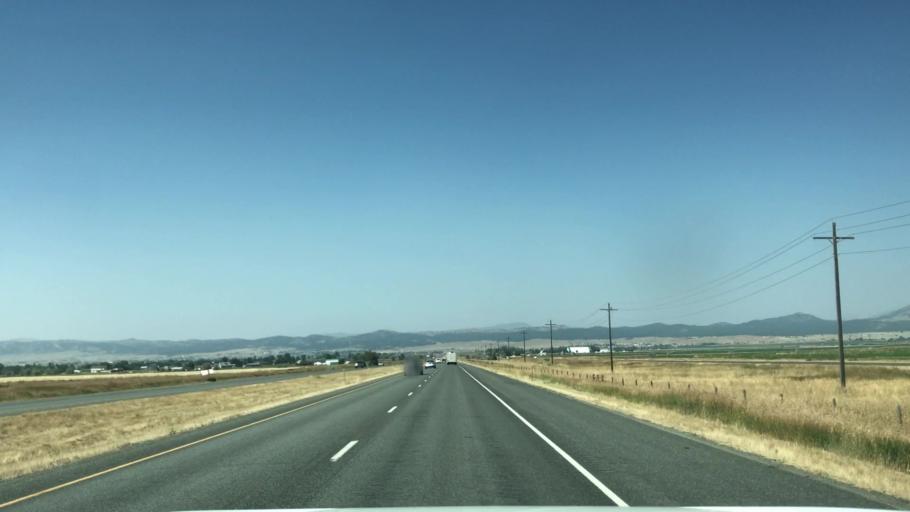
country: US
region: Montana
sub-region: Lewis and Clark County
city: Helena Valley West Central
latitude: 46.6666
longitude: -112.0108
